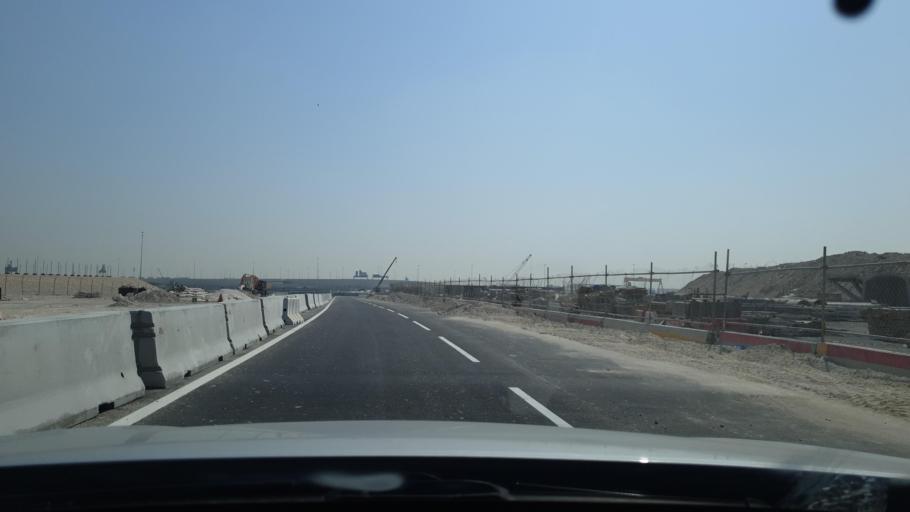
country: QA
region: Baladiyat ad Dawhah
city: Doha
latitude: 25.2237
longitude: 51.5243
